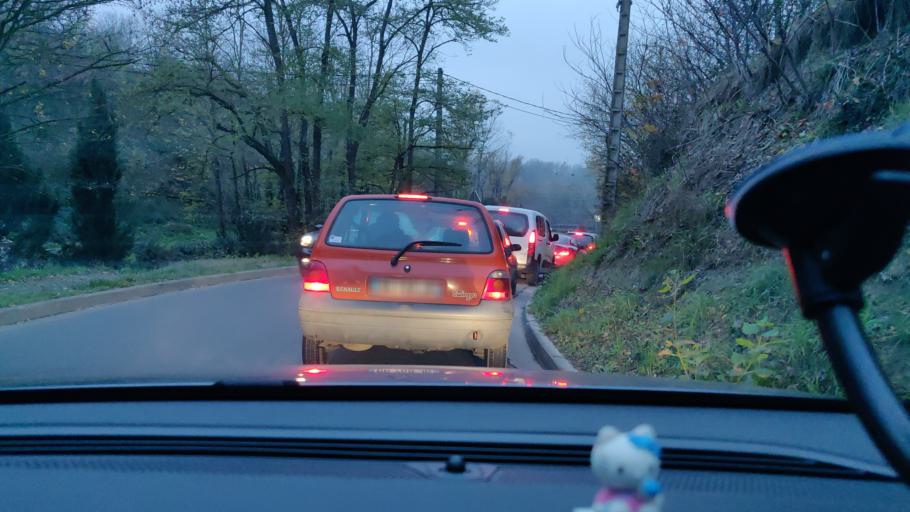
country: FR
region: Midi-Pyrenees
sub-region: Departement de la Haute-Garonne
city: Vieille-Toulouse
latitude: 43.5492
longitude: 1.4414
